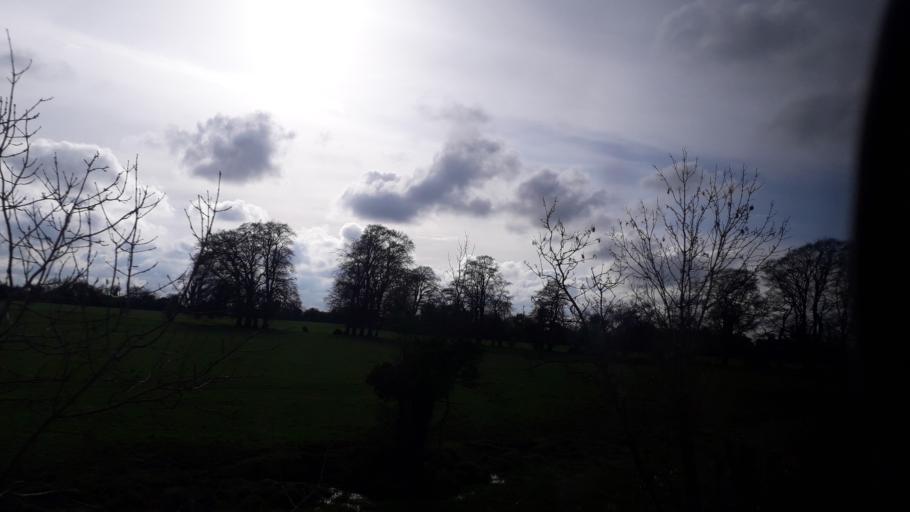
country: IE
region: Leinster
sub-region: An Mhi
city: Longwood
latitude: 53.4403
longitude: -6.9274
